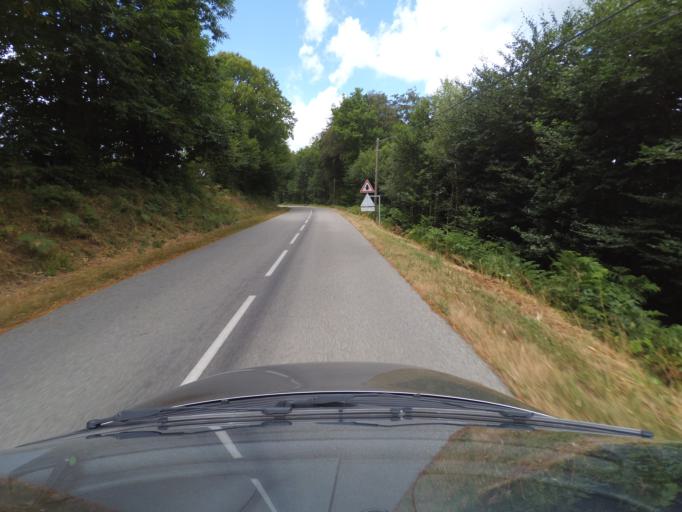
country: FR
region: Limousin
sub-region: Departement de la Creuse
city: Bourganeuf
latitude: 45.9433
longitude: 1.7934
